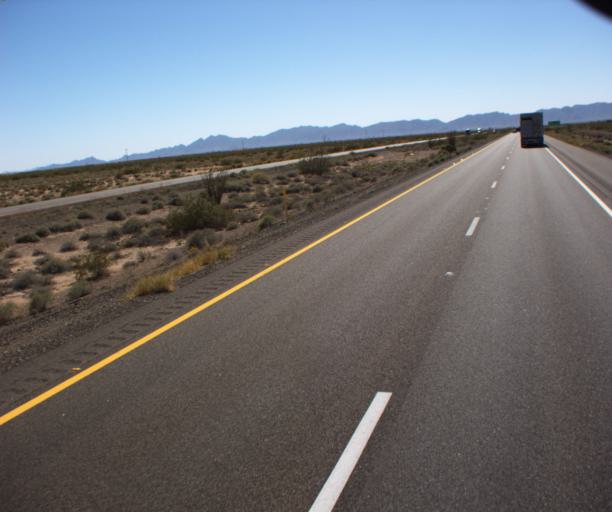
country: US
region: Arizona
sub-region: Yuma County
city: Wellton
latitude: 32.7945
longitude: -113.5524
